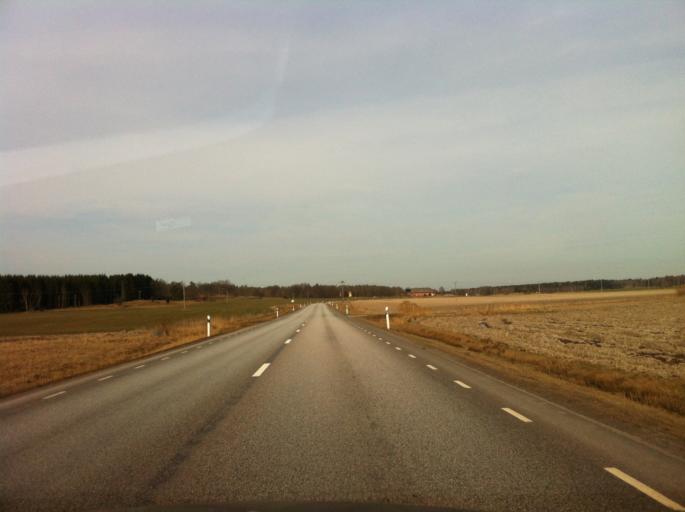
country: SE
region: Vaestra Goetaland
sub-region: Mariestads Kommun
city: Mariestad
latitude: 58.7591
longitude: 13.9471
